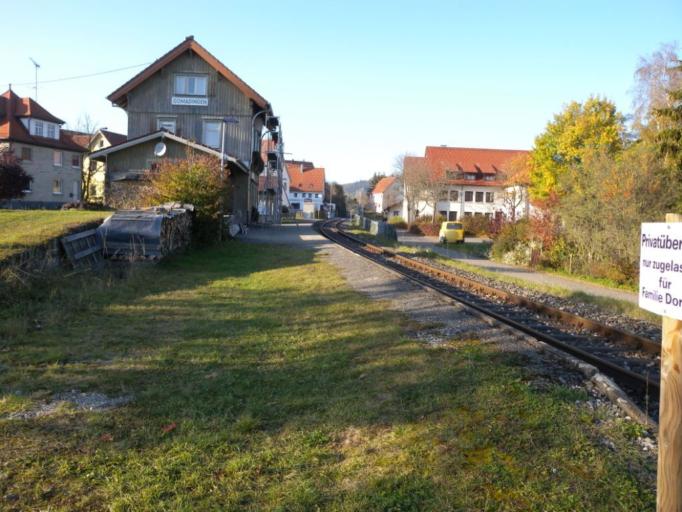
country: DE
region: Baden-Wuerttemberg
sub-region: Tuebingen Region
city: Gomadingen
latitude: 48.3988
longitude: 9.3924
